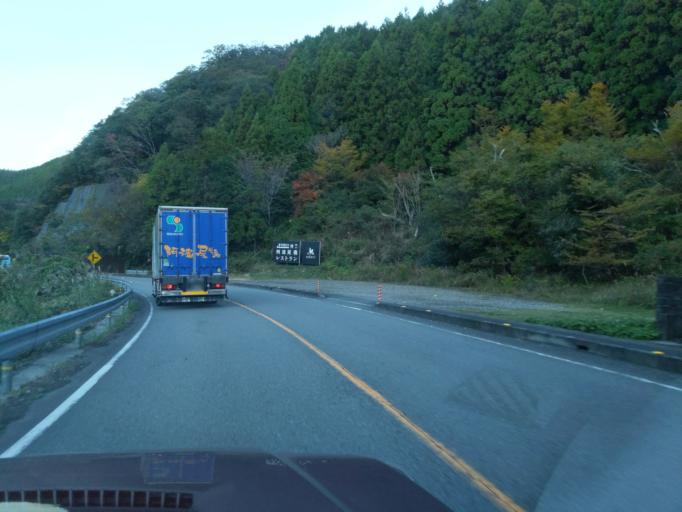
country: JP
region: Tokushima
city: Anan
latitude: 33.7179
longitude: 134.4906
